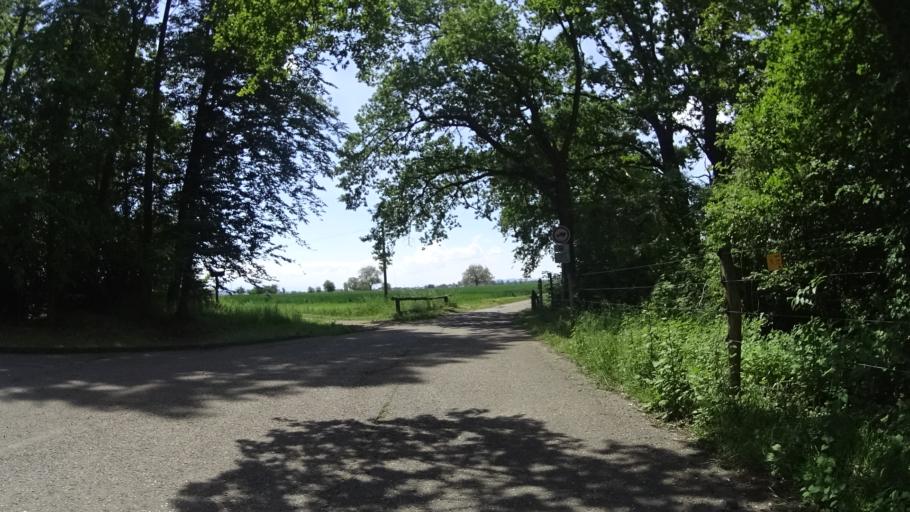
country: DE
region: Baden-Wuerttemberg
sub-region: Freiburg Region
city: Kappel-Grafenhausen
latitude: 48.3121
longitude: 7.7447
